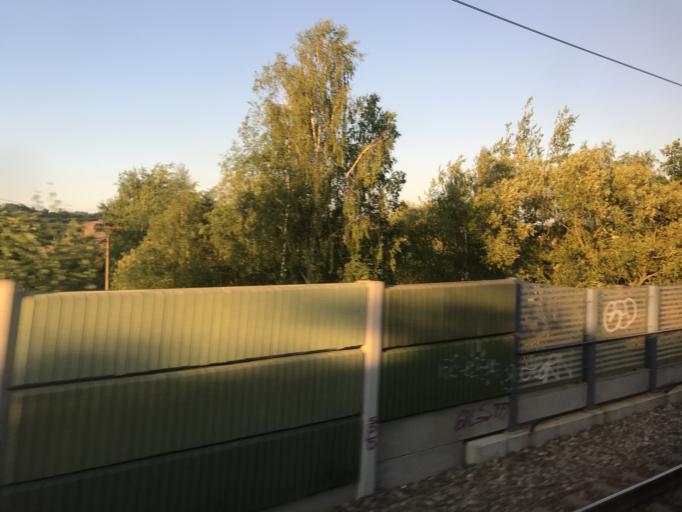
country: CZ
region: Central Bohemia
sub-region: Okres Praha-Vychod
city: Mnichovice
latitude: 49.9091
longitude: 14.7217
